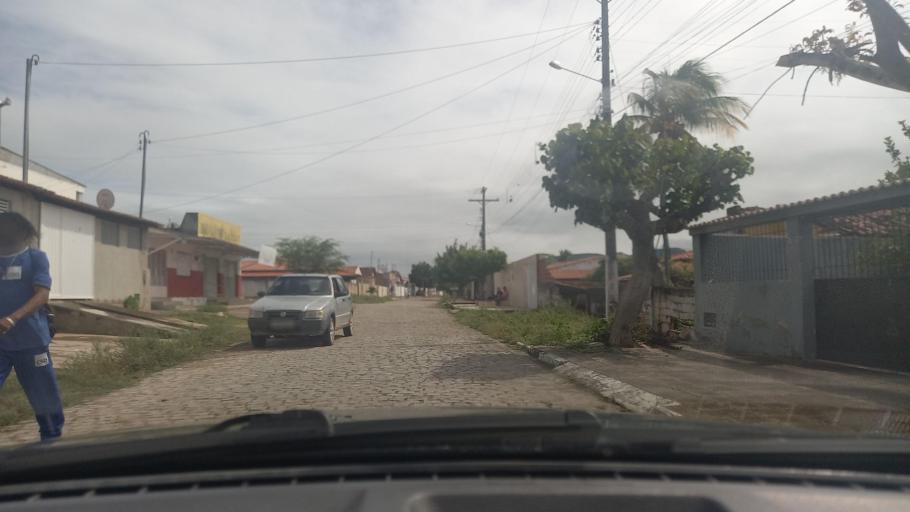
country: BR
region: Bahia
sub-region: Paulo Afonso
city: Paulo Afonso
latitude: -9.3428
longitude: -38.2571
